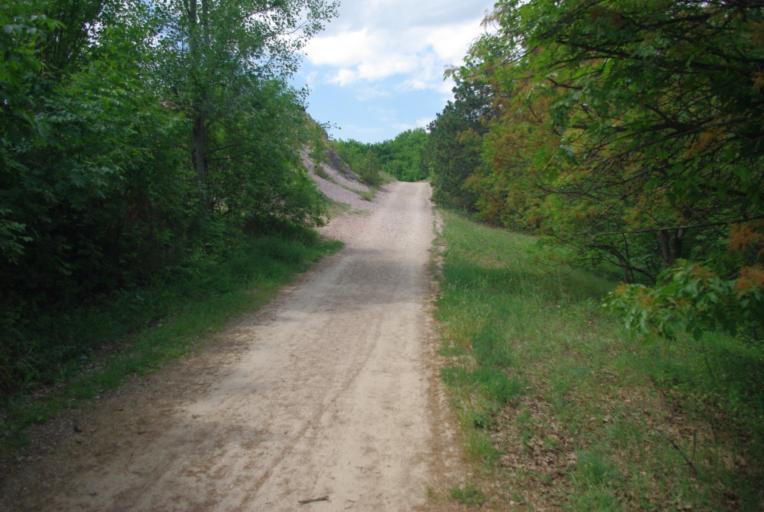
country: HU
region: Pest
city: Pilisszentivan
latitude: 47.5883
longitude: 18.8877
